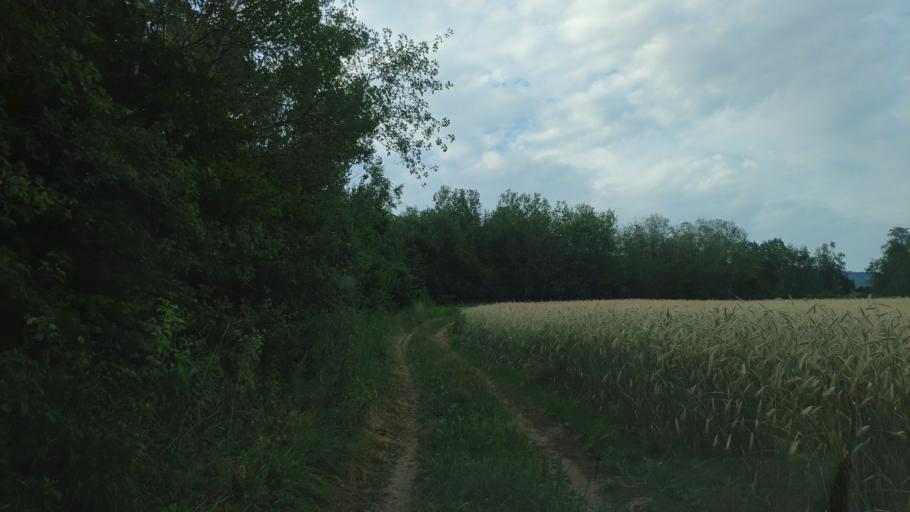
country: SK
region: Kosicky
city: Moldava nad Bodvou
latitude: 48.7084
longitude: 20.9918
